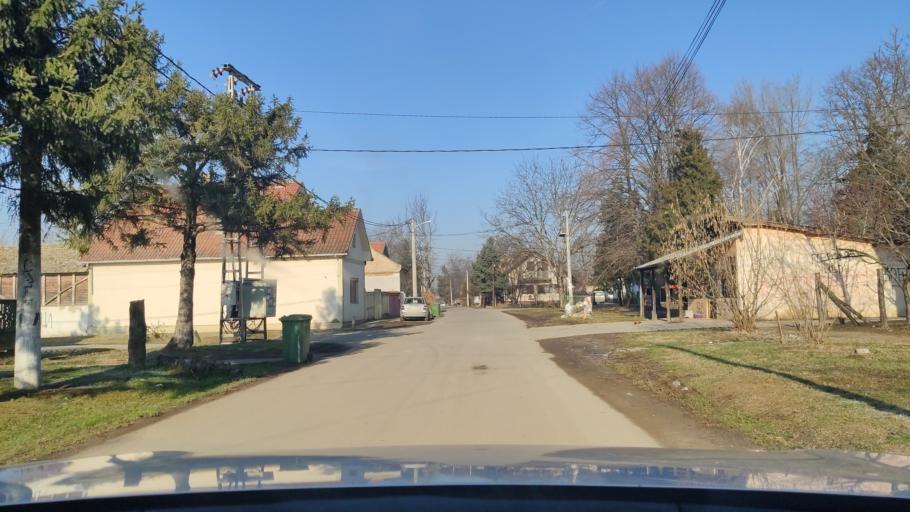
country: RS
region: Central Serbia
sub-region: Belgrade
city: Surcin
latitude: 44.7494
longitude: 20.2684
